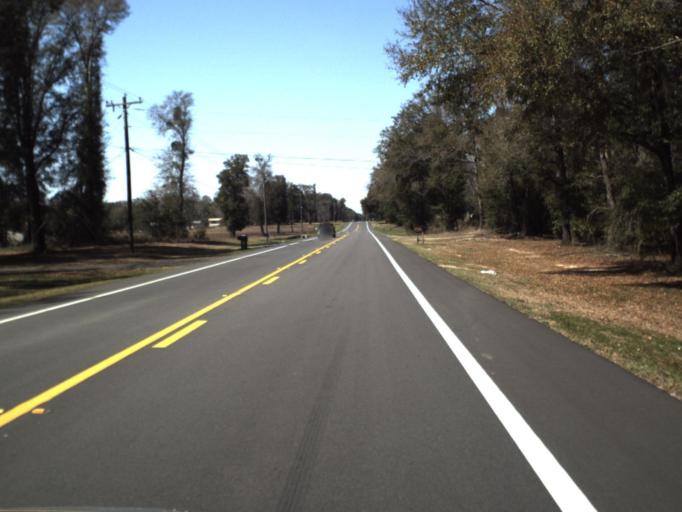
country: US
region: Florida
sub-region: Jackson County
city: Malone
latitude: 30.8641
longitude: -85.1144
